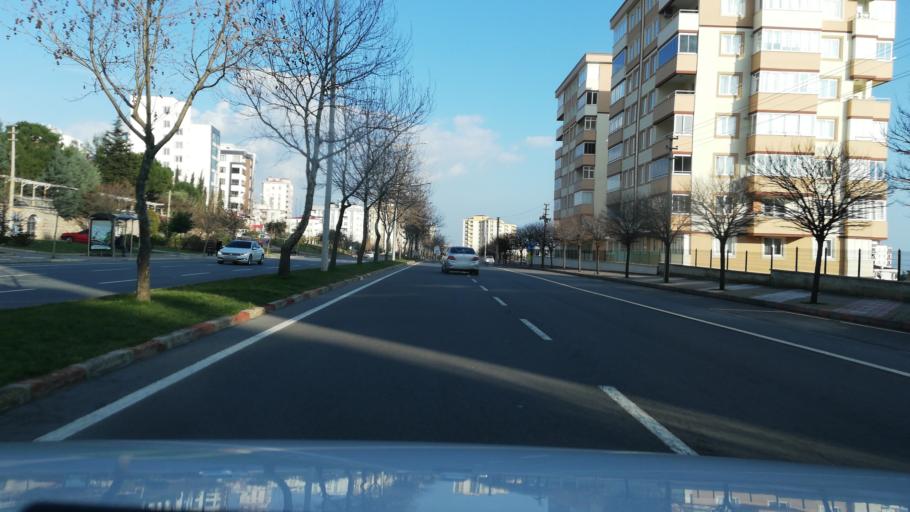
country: TR
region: Kahramanmaras
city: Kahramanmaras
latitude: 37.5957
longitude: 36.8880
